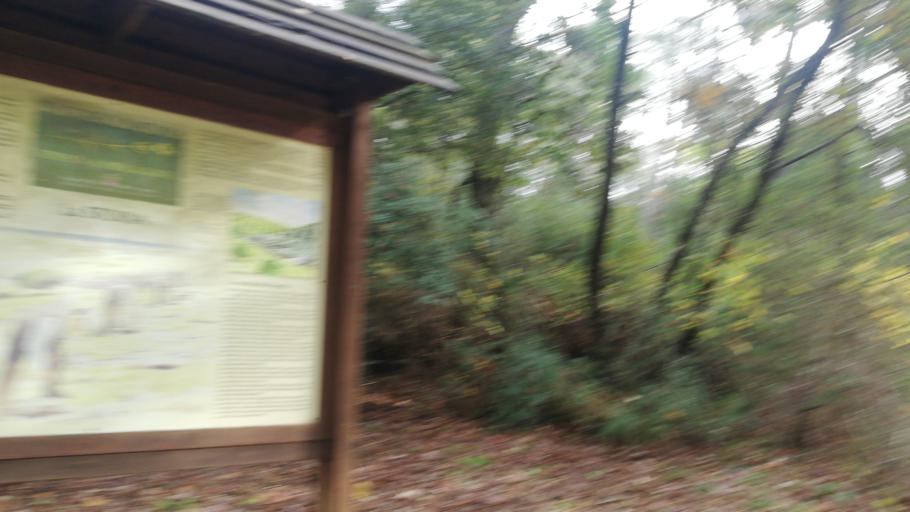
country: IT
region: Apulia
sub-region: Provincia di Bari
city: Cassano delle Murge
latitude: 40.8833
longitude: 16.7063
